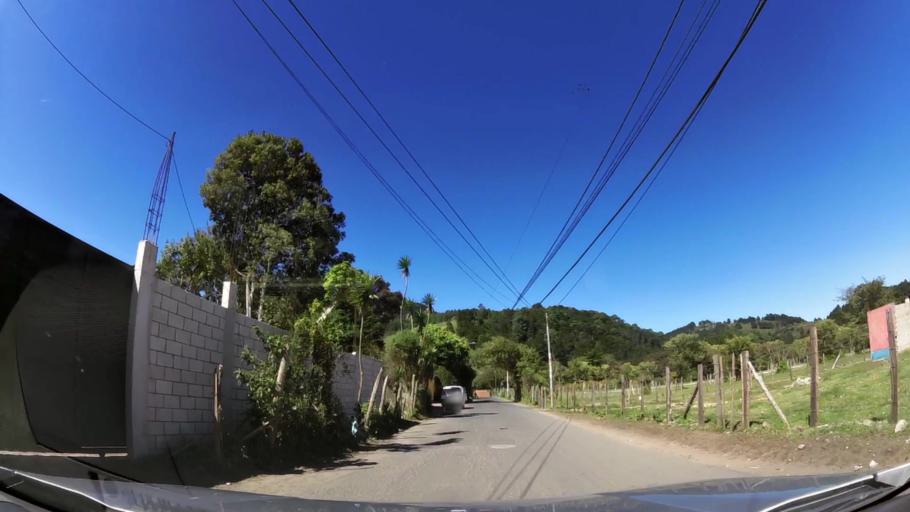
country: GT
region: Guatemala
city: San Jose Pinula
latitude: 14.5279
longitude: -90.4159
